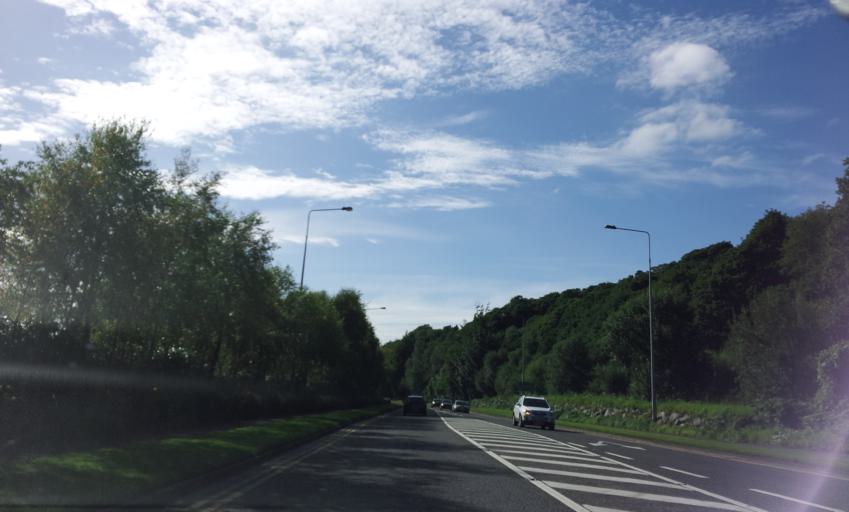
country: IE
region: Munster
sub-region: Ciarrai
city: Cill Airne
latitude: 52.0579
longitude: -9.4724
